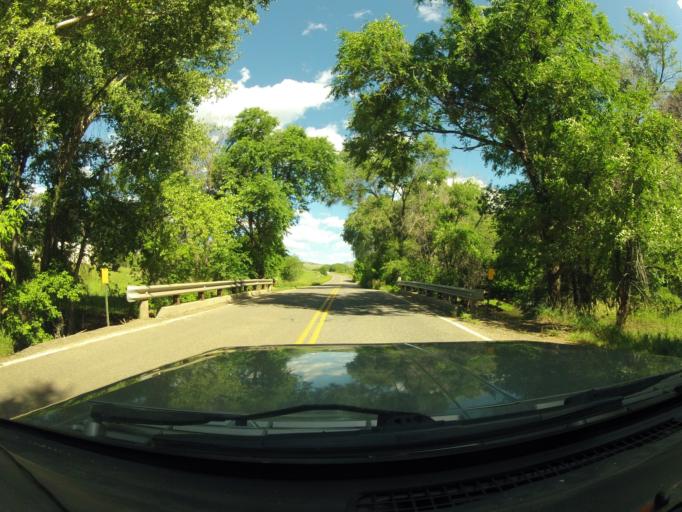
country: US
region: Colorado
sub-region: Larimer County
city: Laporte
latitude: 40.5072
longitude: -105.2406
